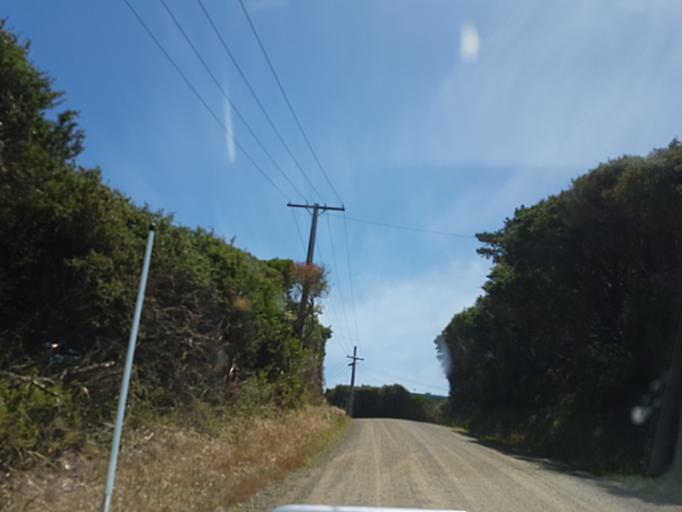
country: AU
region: Victoria
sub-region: Bass Coast
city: North Wonthaggi
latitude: -38.7014
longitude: 145.8284
